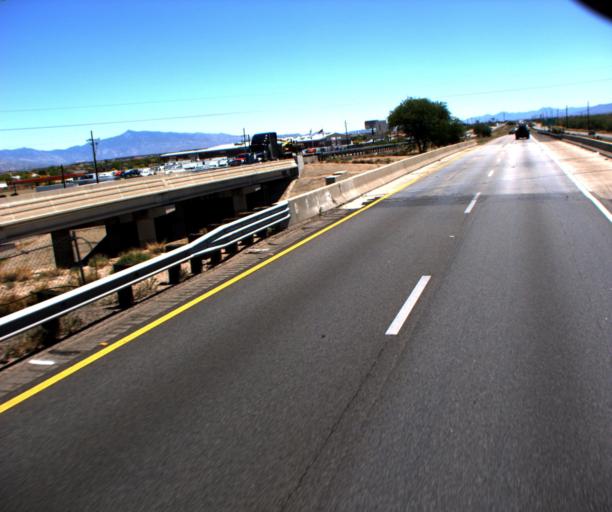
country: US
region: Arizona
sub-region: Pima County
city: Summit
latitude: 32.1254
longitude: -110.8757
